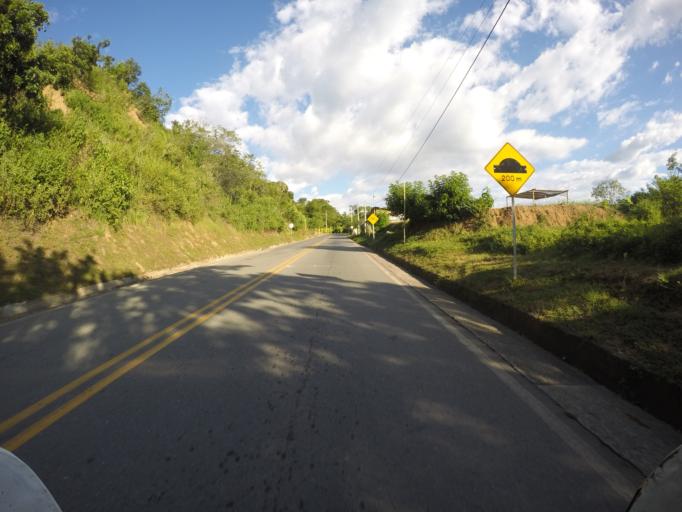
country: CO
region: Valle del Cauca
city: Alcala
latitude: 4.7042
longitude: -75.8503
